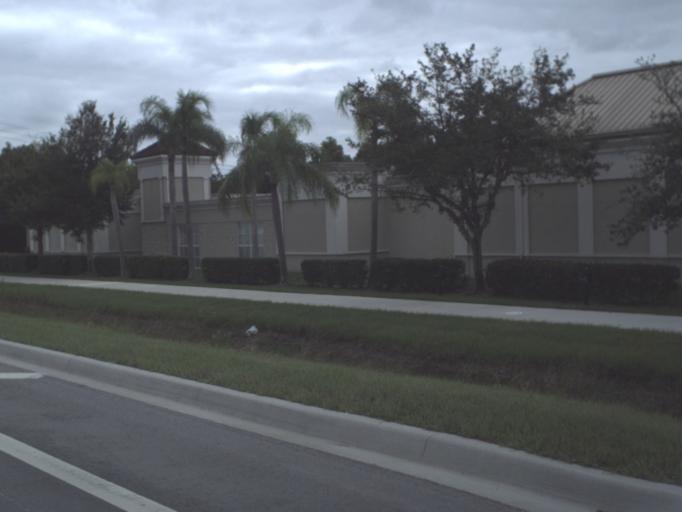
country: US
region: Florida
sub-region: Collier County
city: Lely Resort
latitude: 26.0658
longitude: -81.6972
